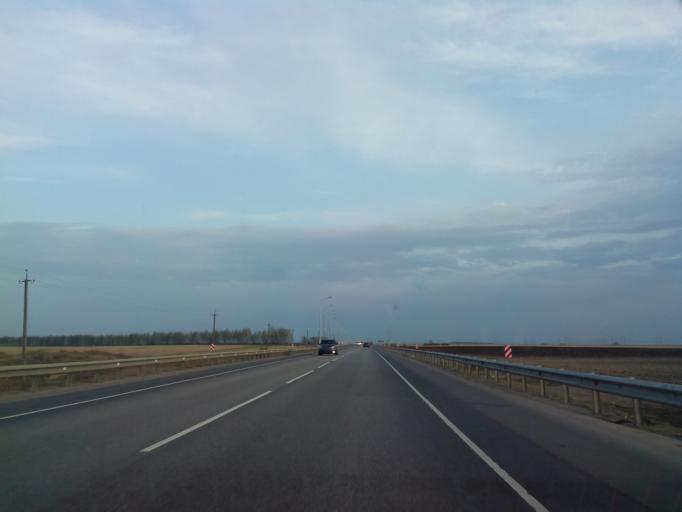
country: RU
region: Rjazan
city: Ryazhsk
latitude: 53.5839
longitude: 40.0409
